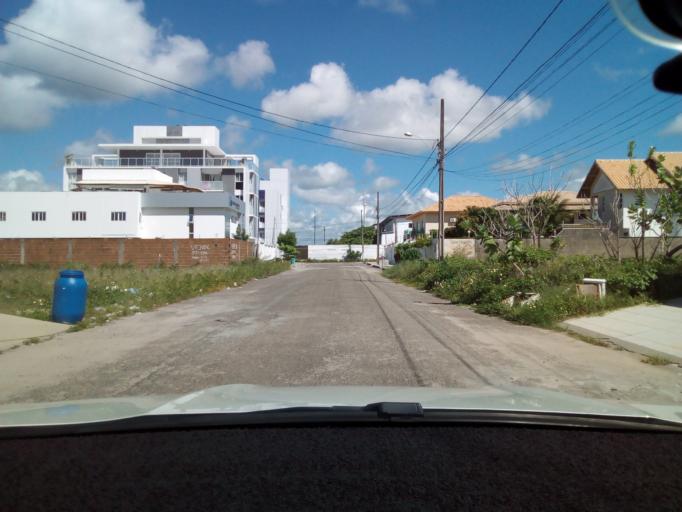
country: BR
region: Paraiba
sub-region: Joao Pessoa
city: Joao Pessoa
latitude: -7.0523
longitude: -34.8483
